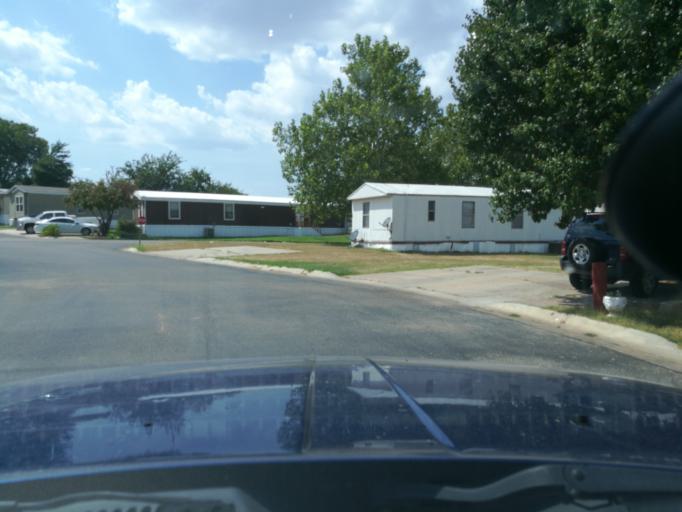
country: US
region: Oklahoma
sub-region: Oklahoma County
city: Del City
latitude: 35.4176
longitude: -97.4718
